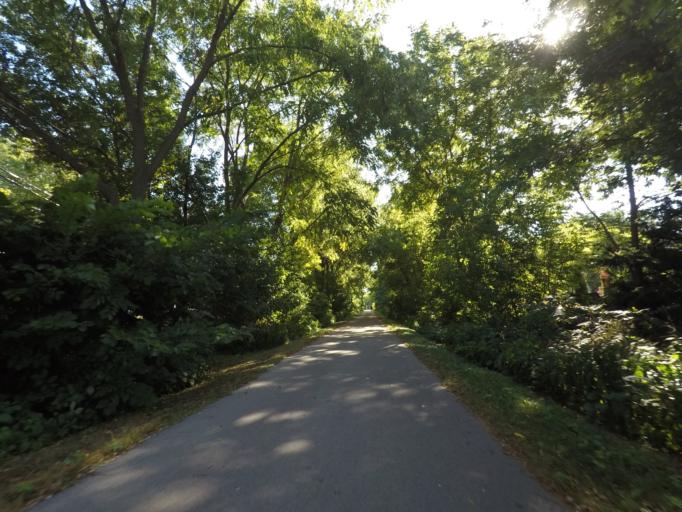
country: US
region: Wisconsin
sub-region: Waukesha County
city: Waukesha
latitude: 43.0083
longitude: -88.2147
